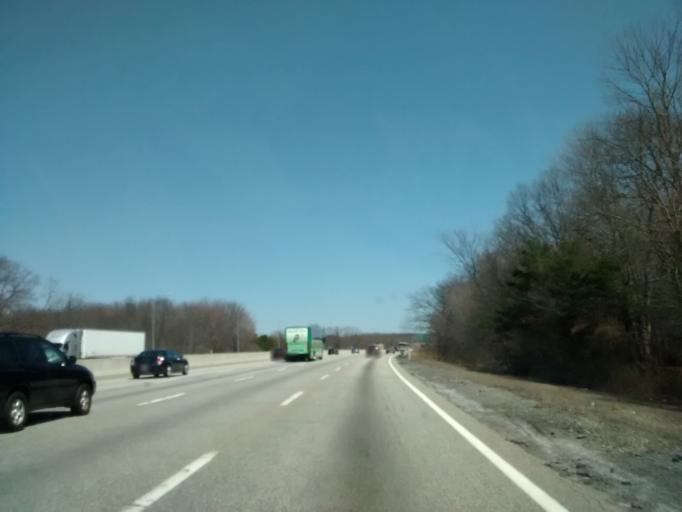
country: US
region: Massachusetts
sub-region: Worcester County
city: Westborough
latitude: 42.2613
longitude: -71.5752
